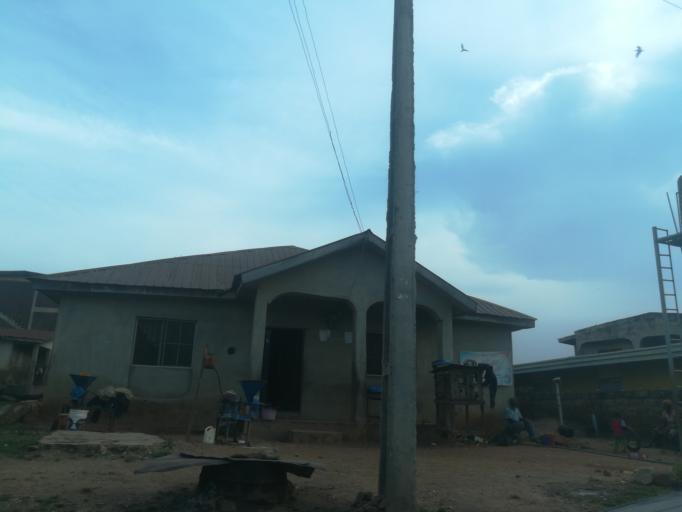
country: NG
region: Oyo
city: Moniya
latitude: 7.5303
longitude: 3.9098
